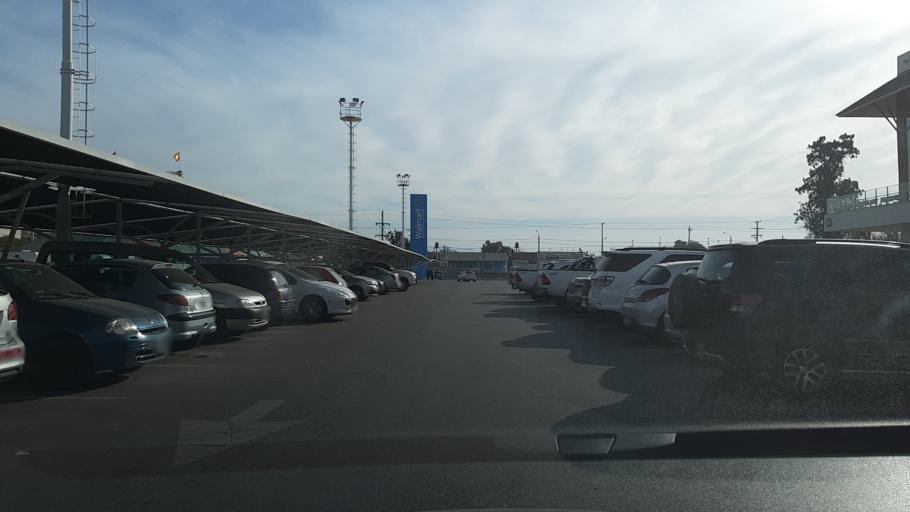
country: AR
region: San Juan
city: San Juan
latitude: -31.5400
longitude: -68.5732
